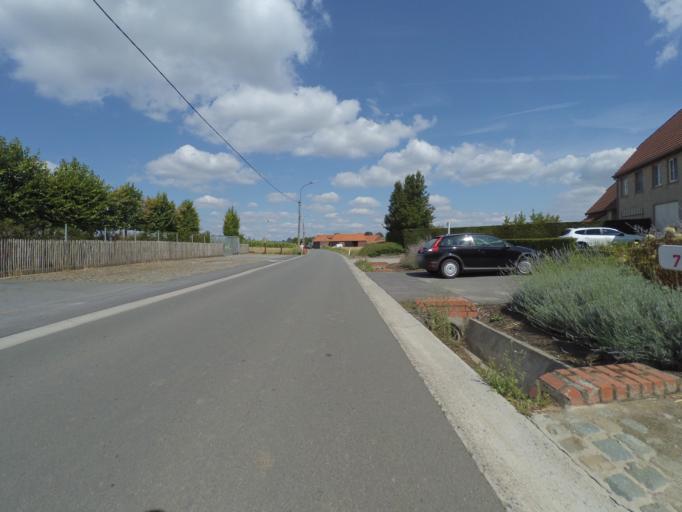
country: BE
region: Wallonia
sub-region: Province du Hainaut
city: Ellezelles
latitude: 50.7946
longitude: 3.6752
